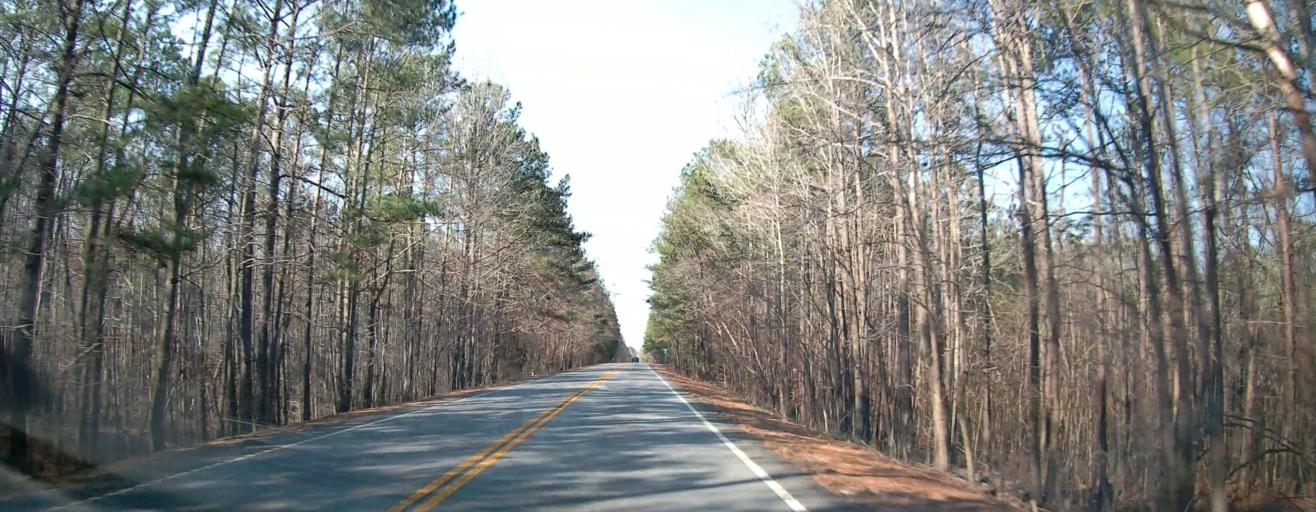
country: US
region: Georgia
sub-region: Butts County
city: Indian Springs
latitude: 33.1574
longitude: -83.8400
